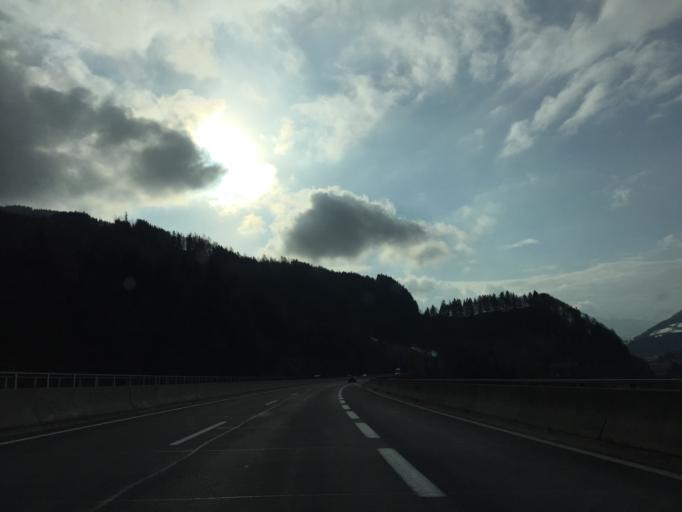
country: AT
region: Salzburg
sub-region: Politischer Bezirk Sankt Johann im Pongau
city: Werfen
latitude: 47.4862
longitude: 13.1914
